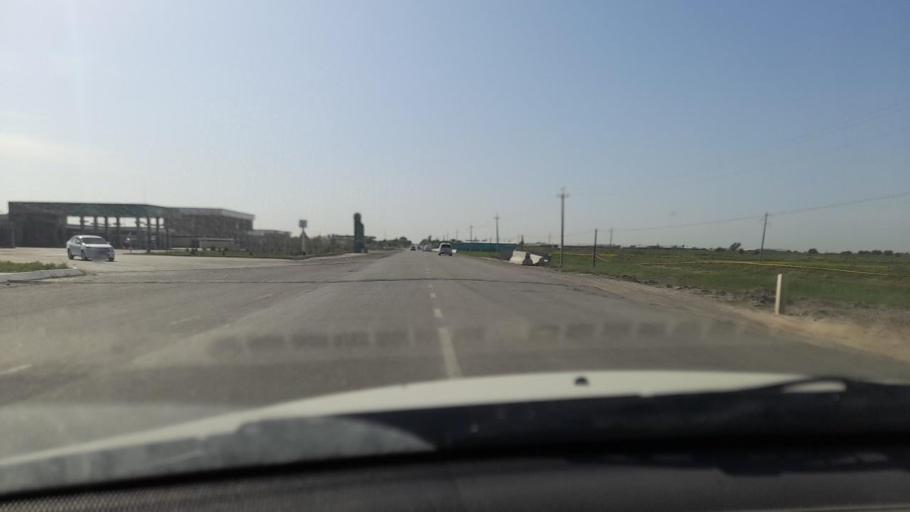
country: UZ
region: Bukhara
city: Romiton
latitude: 39.9165
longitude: 64.3899
